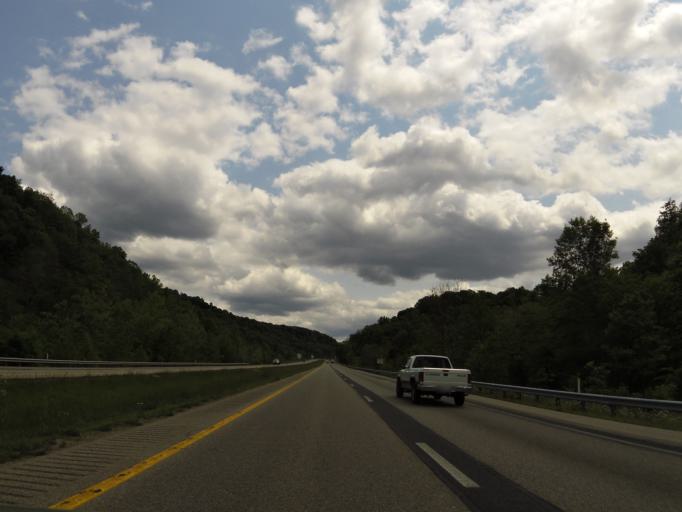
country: US
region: West Virginia
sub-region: Kanawha County
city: Sissonville
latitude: 38.4531
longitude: -81.6363
